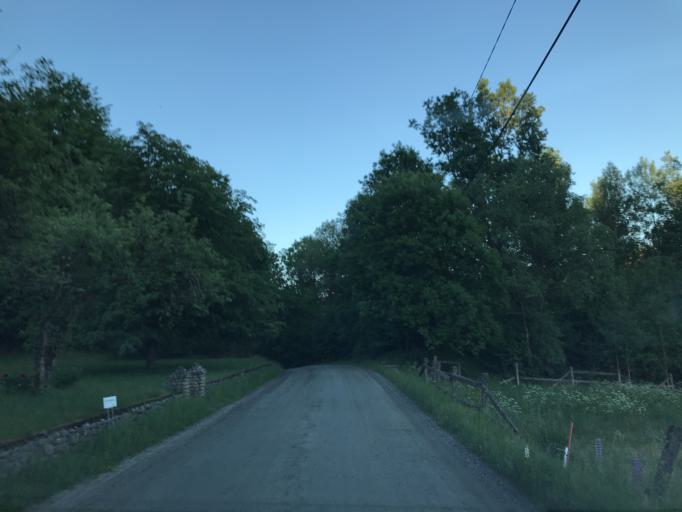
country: SE
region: Vaestra Goetaland
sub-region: Bollebygds Kommun
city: Bollebygd
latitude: 57.7503
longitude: 12.6078
